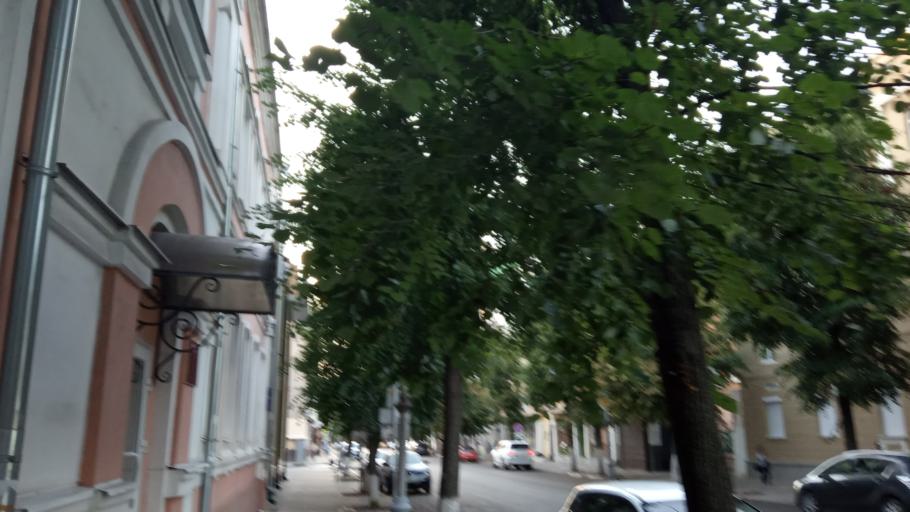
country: RU
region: Voronezj
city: Voronezh
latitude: 51.6613
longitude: 39.2073
